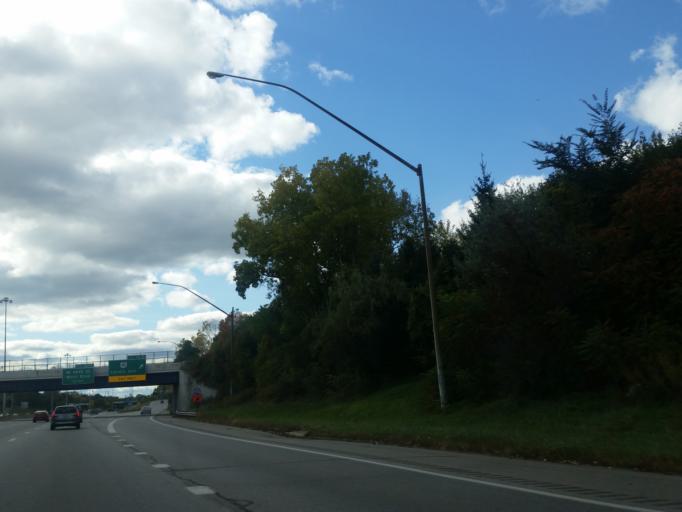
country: US
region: Ohio
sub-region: Cuyahoga County
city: Brooklyn
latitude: 41.4714
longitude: -81.7342
